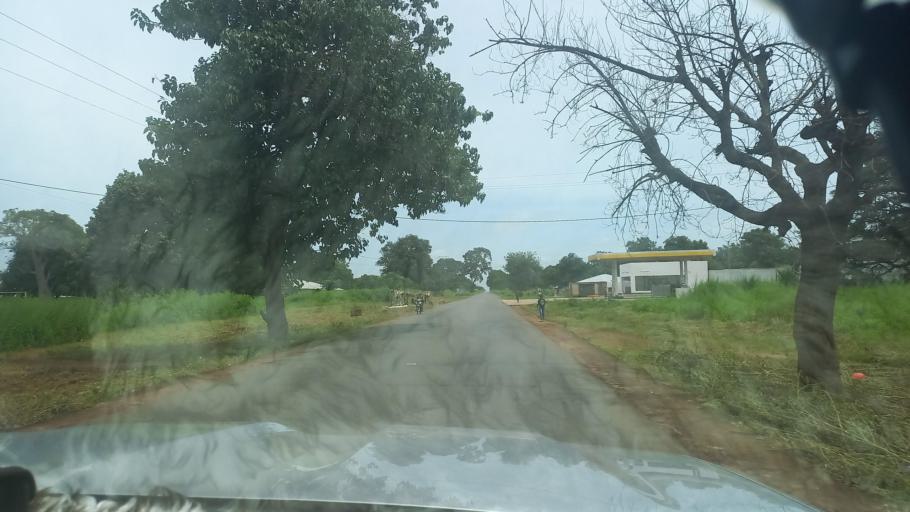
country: SN
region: Kolda
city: Marsassoum
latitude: 12.9611
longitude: -15.9897
